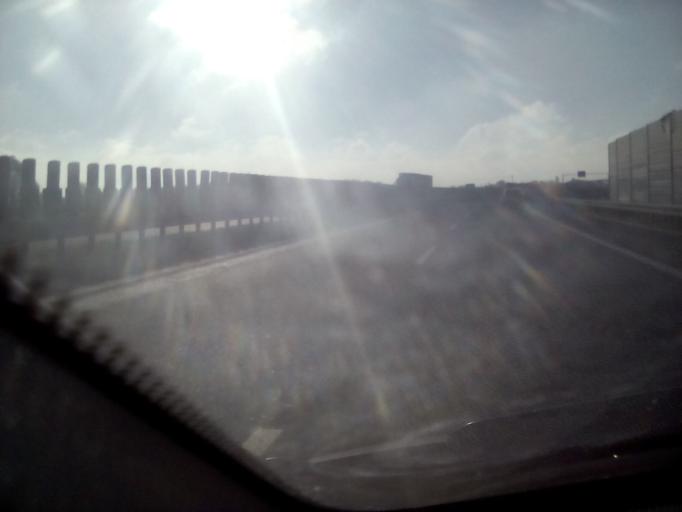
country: PL
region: Masovian Voivodeship
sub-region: Powiat grojecki
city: Grojec
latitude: 51.8448
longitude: 20.8732
